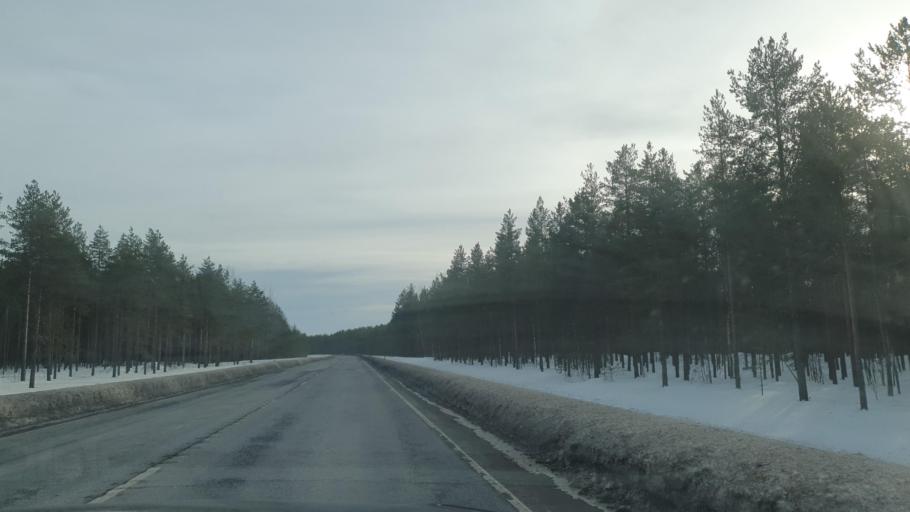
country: FI
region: Northern Ostrobothnia
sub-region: Oulunkaari
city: Utajaervi
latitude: 64.7113
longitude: 26.5153
